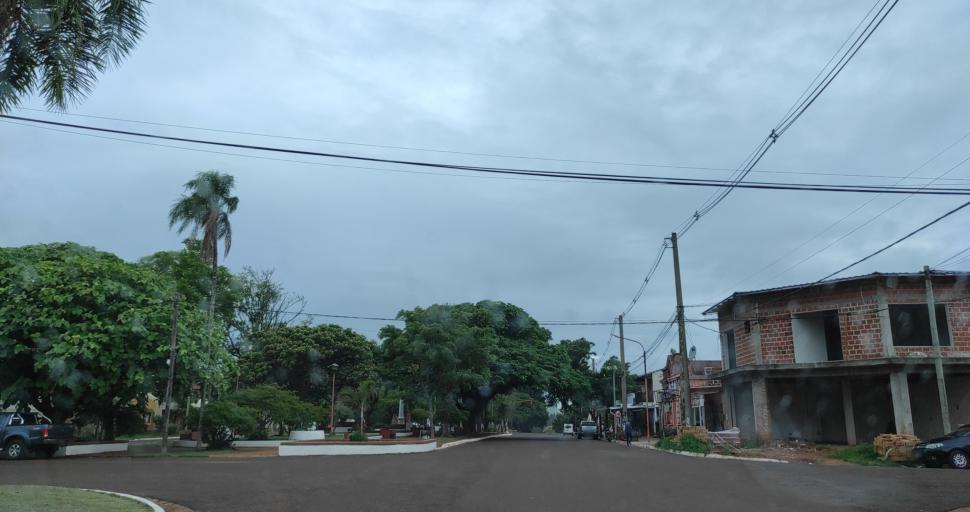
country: AR
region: Misiones
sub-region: Departamento de Apostoles
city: San Jose
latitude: -27.7686
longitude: -55.7785
